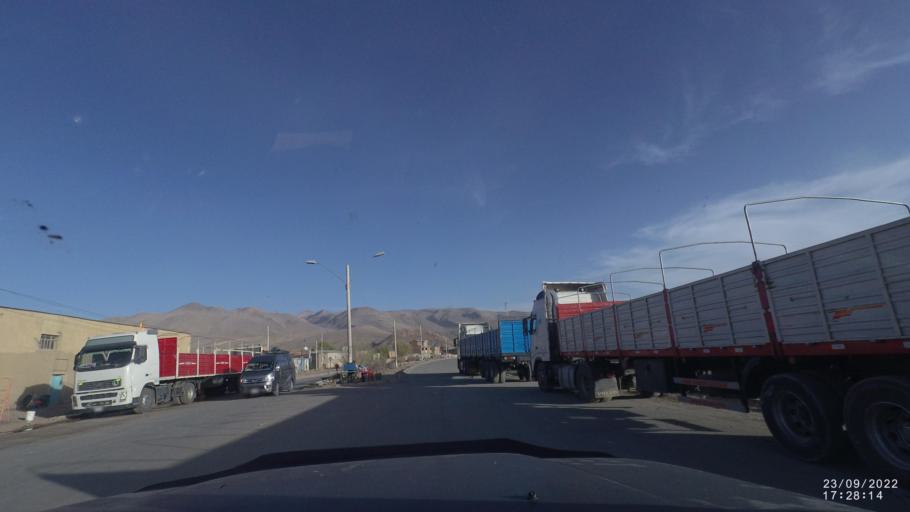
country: BO
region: Oruro
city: Challapata
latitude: -18.8949
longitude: -66.7777
